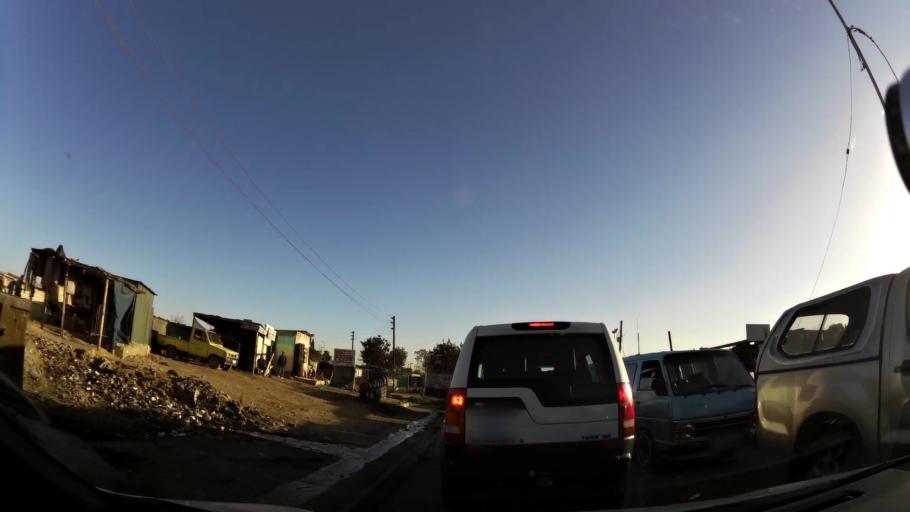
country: ZA
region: Gauteng
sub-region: City of Johannesburg Metropolitan Municipality
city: Diepsloot
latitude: -25.9318
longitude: 28.0154
